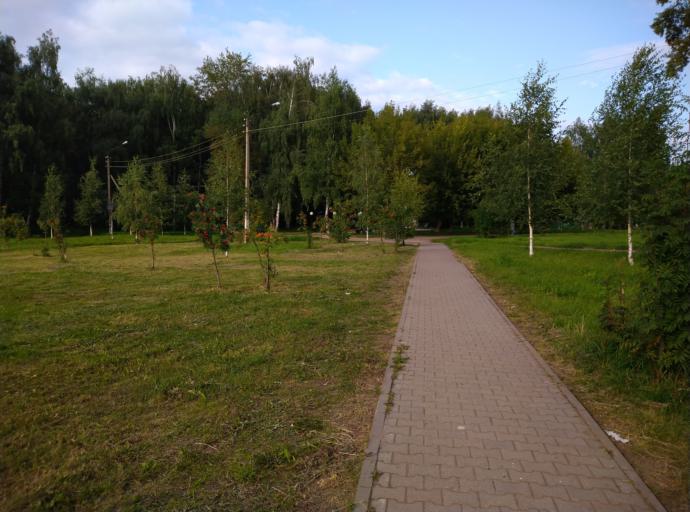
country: RU
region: Kostroma
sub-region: Kostromskoy Rayon
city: Kostroma
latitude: 57.7600
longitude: 40.9624
